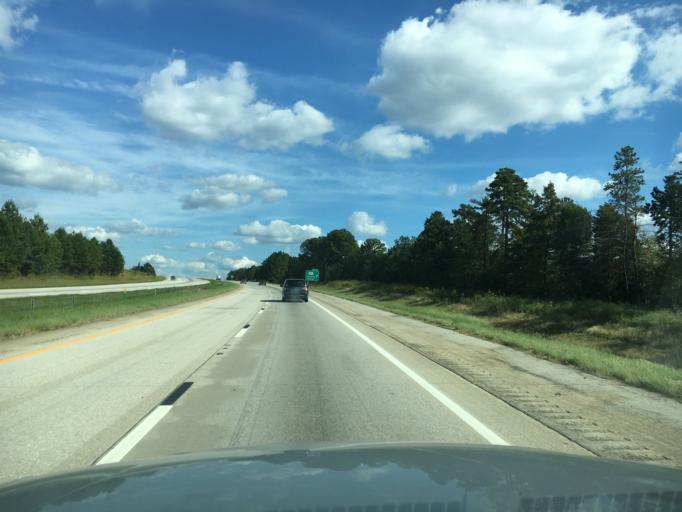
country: US
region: South Carolina
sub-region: Laurens County
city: Watts Mills
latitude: 34.5545
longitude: -82.0133
